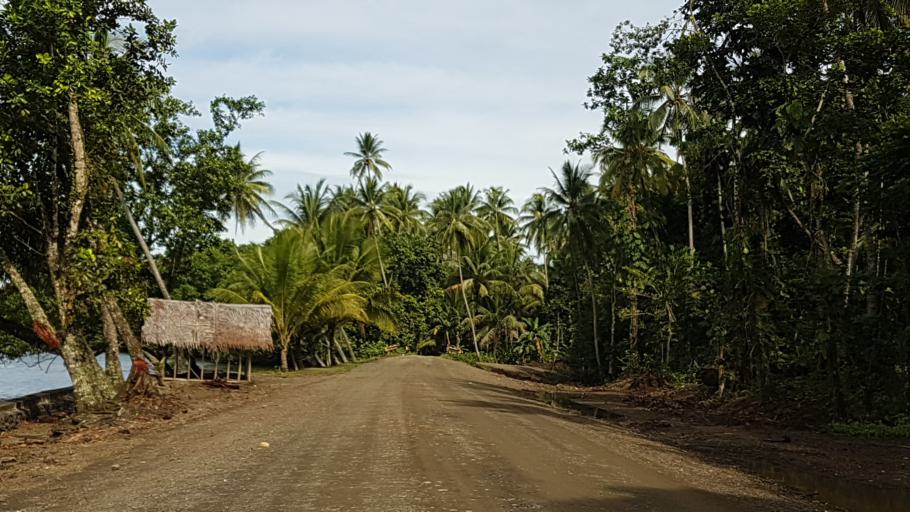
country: PG
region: Milne Bay
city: Alotau
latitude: -10.3436
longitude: 150.5572
